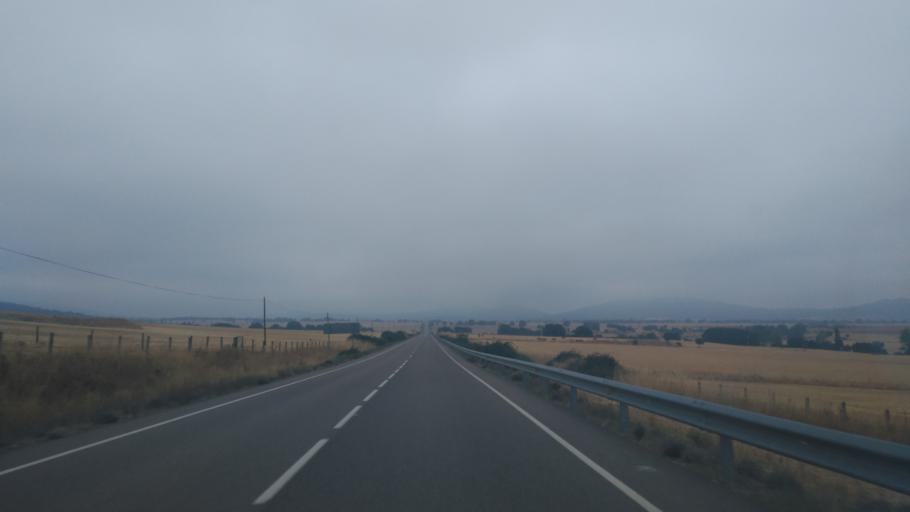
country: ES
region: Castille and Leon
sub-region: Provincia de Salamanca
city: Tamames
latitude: 40.6530
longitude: -6.1168
